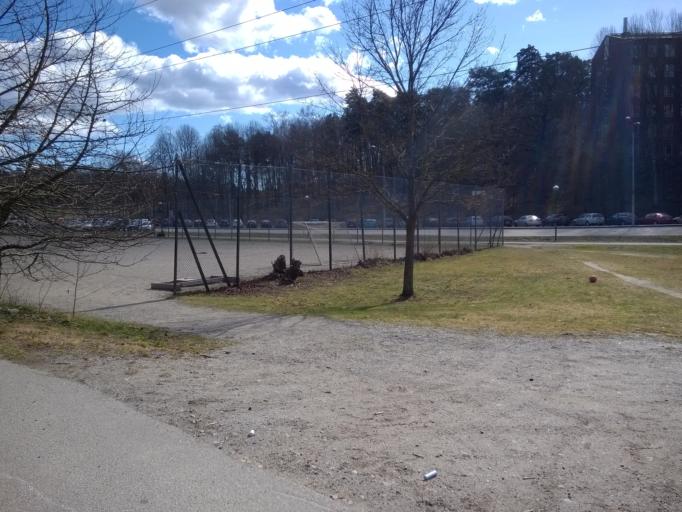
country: SE
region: Stockholm
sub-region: Norrtalje Kommun
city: Bergshamra
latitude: 59.3707
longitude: 18.0552
